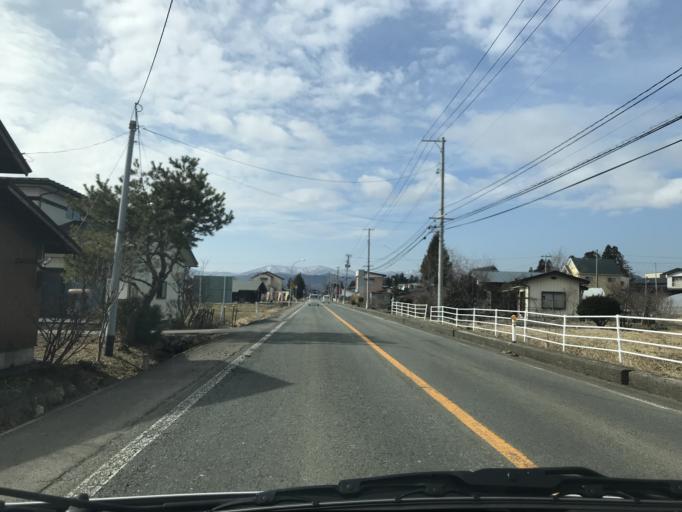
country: JP
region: Iwate
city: Hanamaki
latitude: 39.3826
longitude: 141.0740
